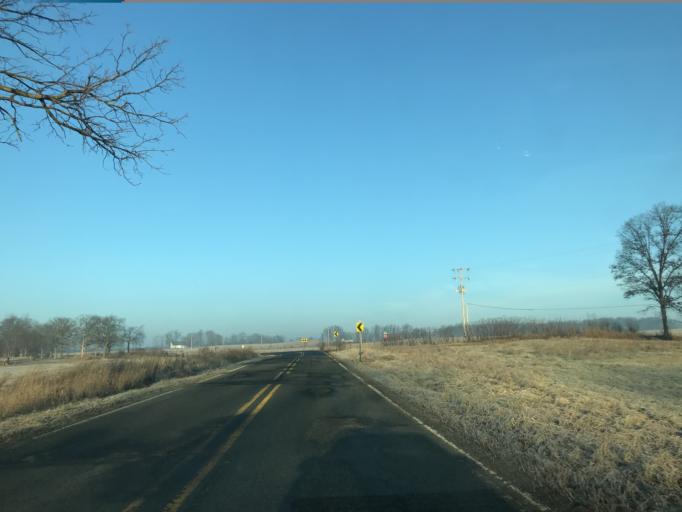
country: US
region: Michigan
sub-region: Ingham County
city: Leslie
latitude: 42.4213
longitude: -84.5166
